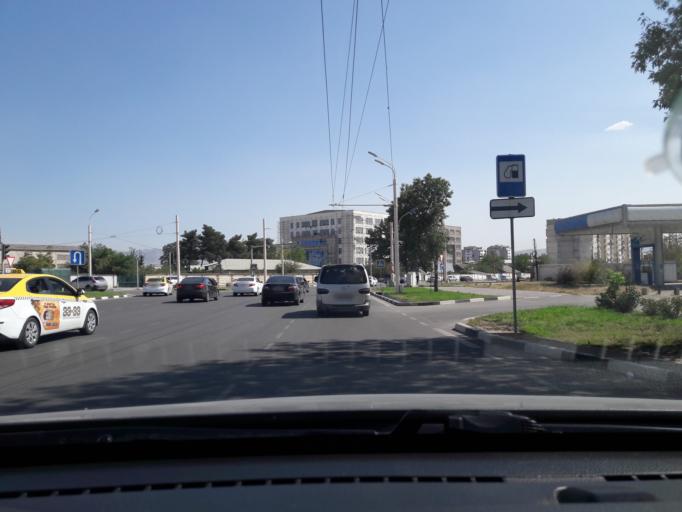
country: TJ
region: Dushanbe
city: Dushanbe
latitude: 38.5370
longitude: 68.7408
